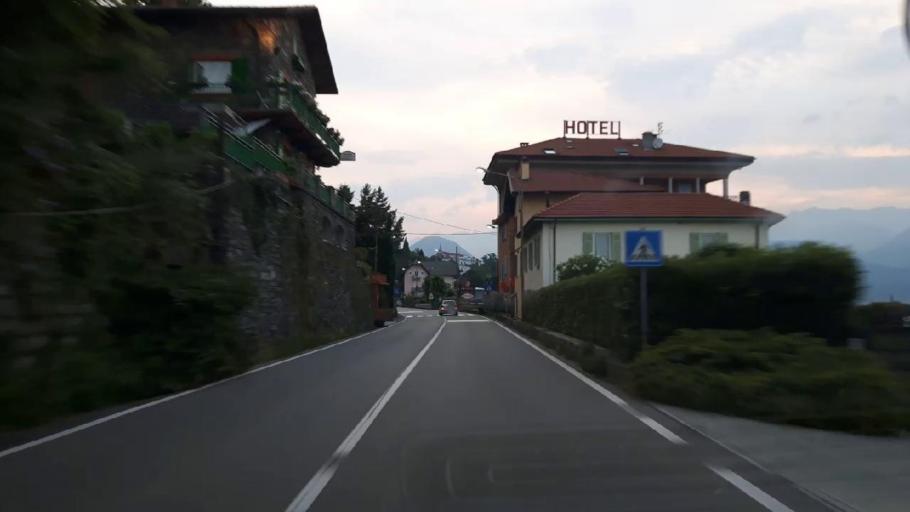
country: IT
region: Piedmont
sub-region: Provincia Verbano-Cusio-Ossola
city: Baveno
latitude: 45.8987
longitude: 8.5121
